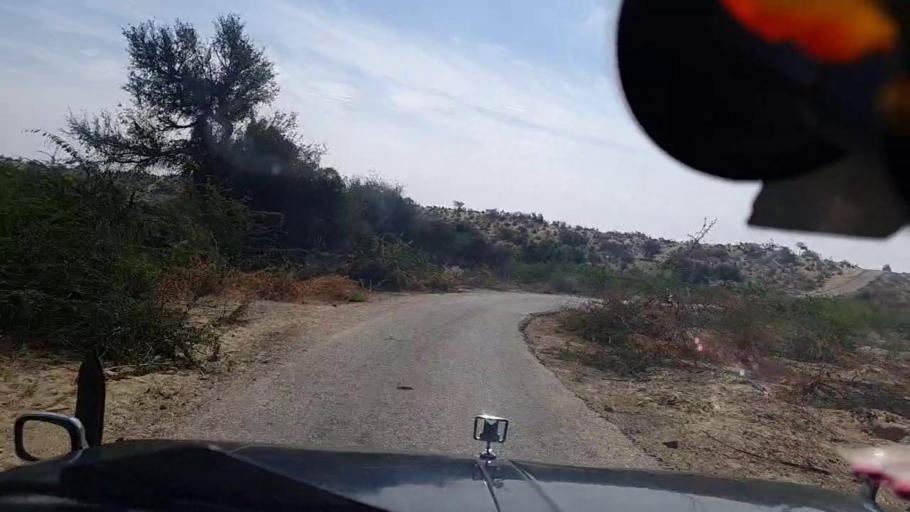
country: PK
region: Sindh
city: Diplo
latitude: 24.4044
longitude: 69.5876
